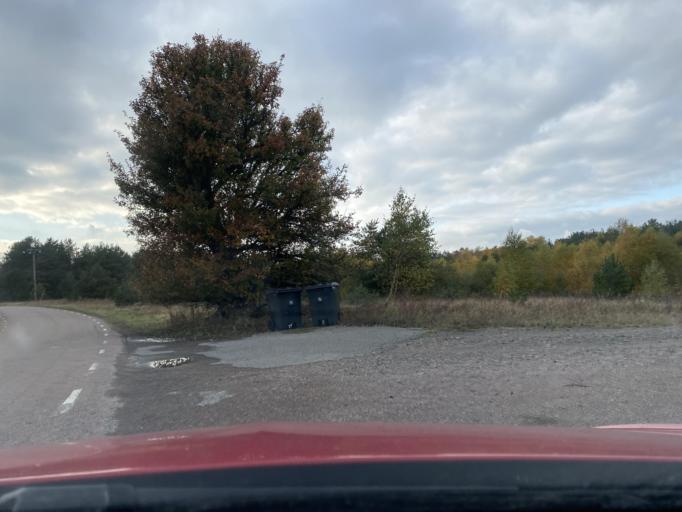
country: SE
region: Skane
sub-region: Hassleholms Kommun
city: Tormestorp
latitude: 56.0241
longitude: 13.7659
